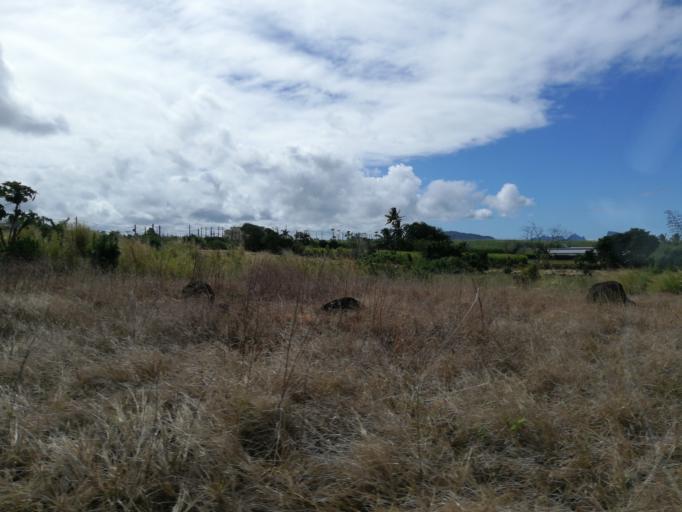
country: MU
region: Grand Port
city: Plaine Magnien
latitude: -20.4447
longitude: 57.6536
